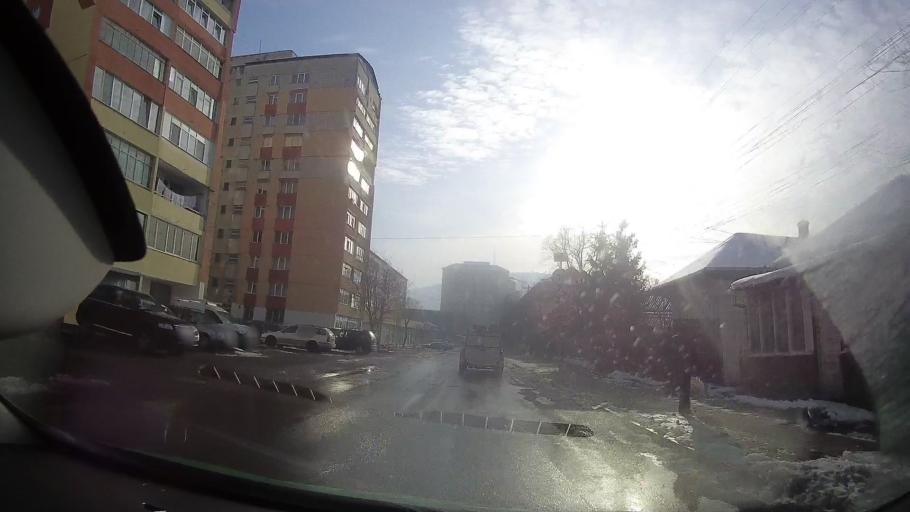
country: RO
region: Neamt
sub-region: Municipiul Piatra-Neamt
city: Valeni
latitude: 46.9418
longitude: 26.3822
